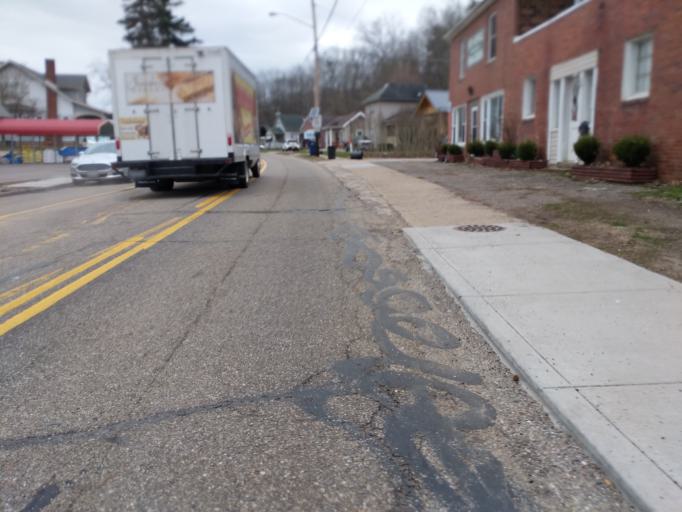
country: US
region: Ohio
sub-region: Athens County
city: Athens
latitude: 39.3096
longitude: -82.1045
